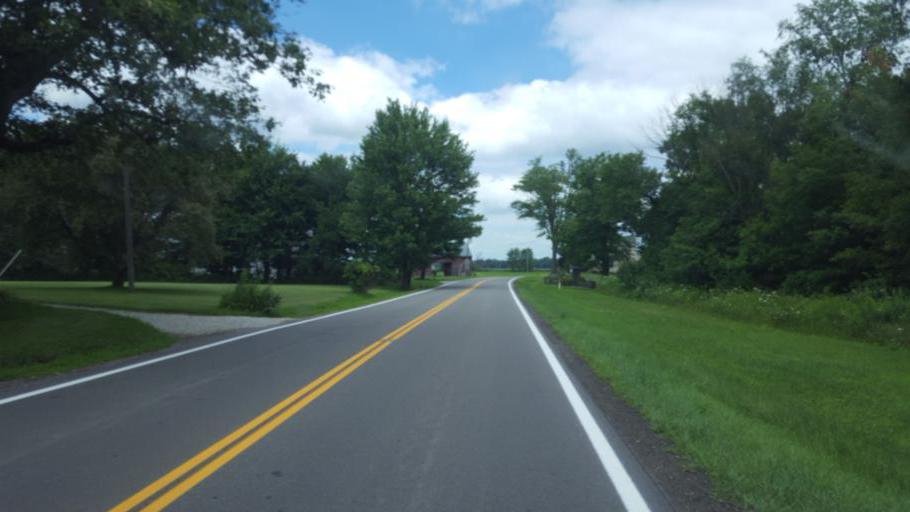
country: US
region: Ohio
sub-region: Richland County
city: Shelby
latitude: 40.8131
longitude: -82.6580
